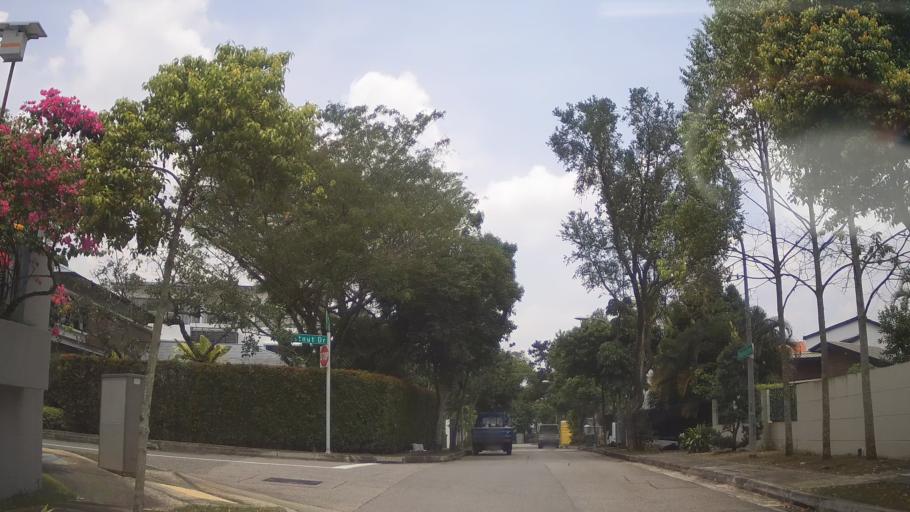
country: MY
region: Johor
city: Johor Bahru
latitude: 1.3716
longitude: 103.7720
